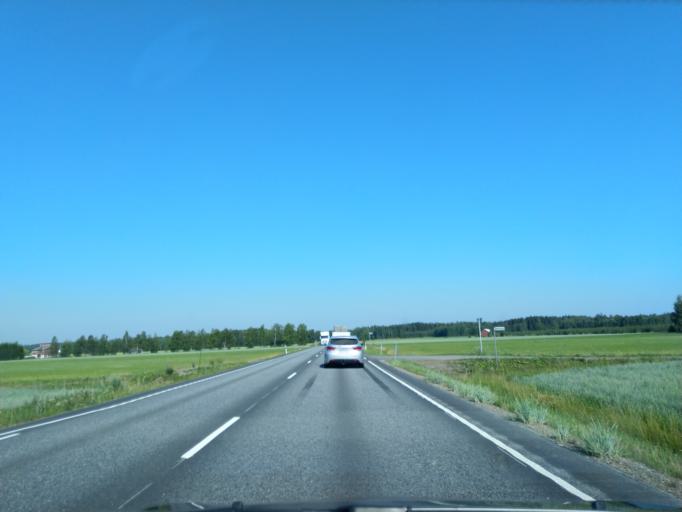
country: FI
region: Varsinais-Suomi
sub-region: Loimaa
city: Alastaro
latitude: 61.0930
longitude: 22.8770
